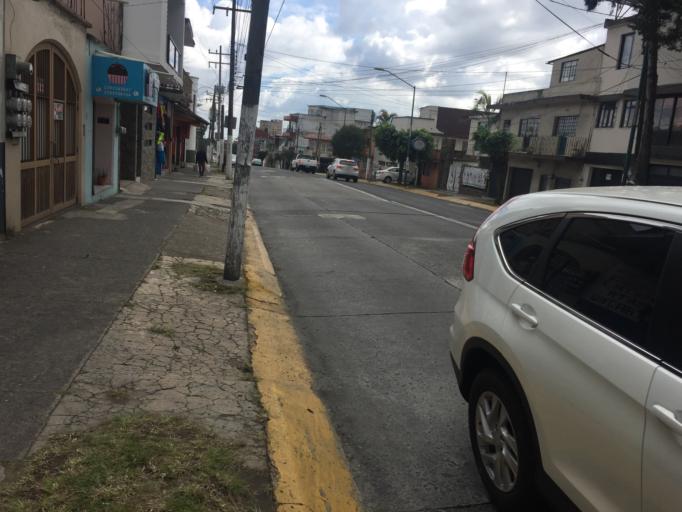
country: MX
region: Veracruz
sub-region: Xalapa
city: Xalapa de Enriquez
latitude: 19.5369
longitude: -96.9224
